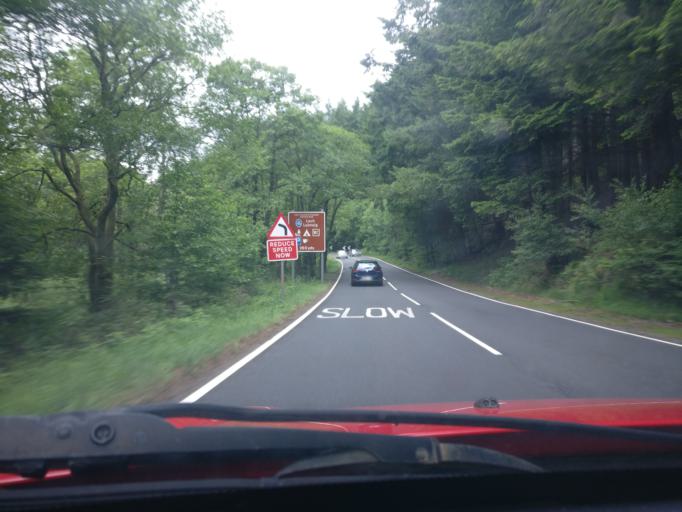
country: GB
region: Scotland
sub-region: Stirling
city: Callander
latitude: 56.2753
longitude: -4.2822
